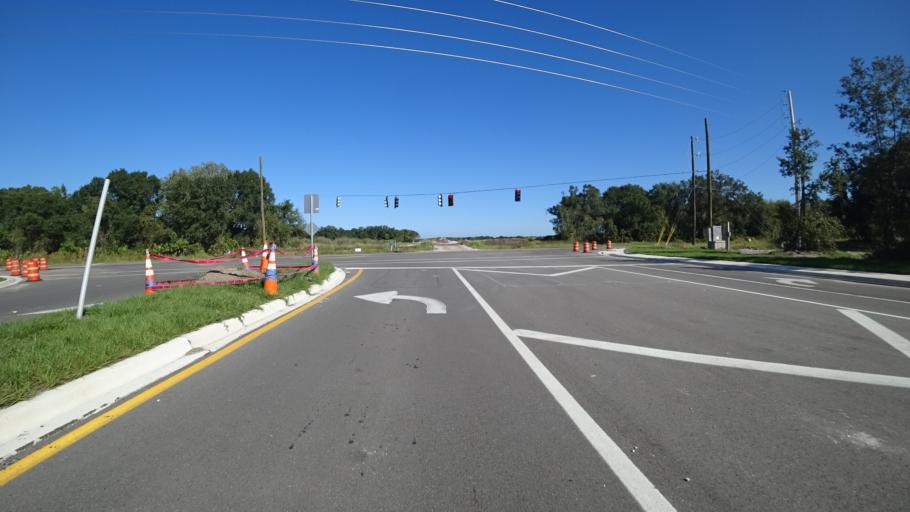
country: US
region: Florida
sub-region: Manatee County
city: Ellenton
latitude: 27.5850
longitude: -82.4356
